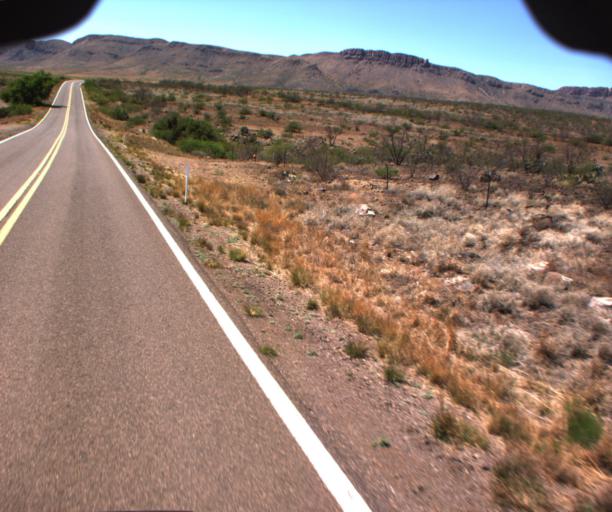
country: US
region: Arizona
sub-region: Cochise County
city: Douglas
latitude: 31.4671
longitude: -109.3616
